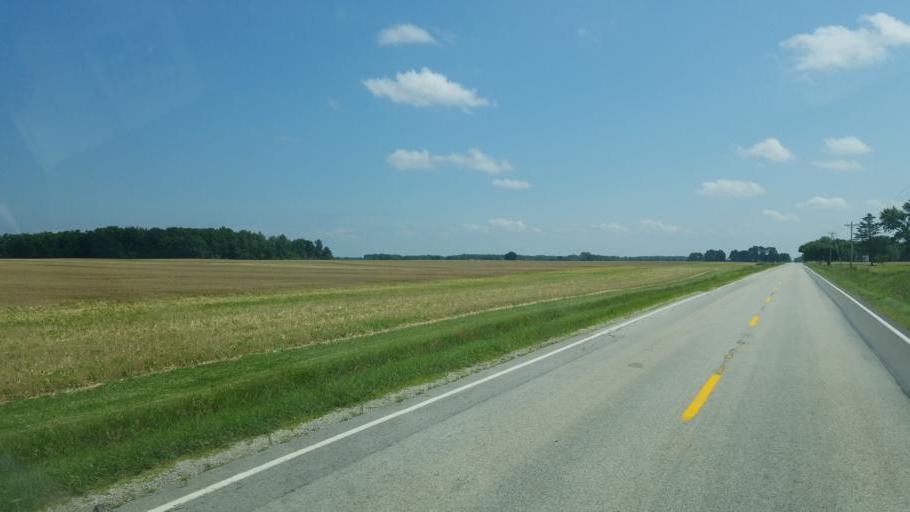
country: US
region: Ohio
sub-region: Huron County
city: Bellevue
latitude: 41.2374
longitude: -82.8395
